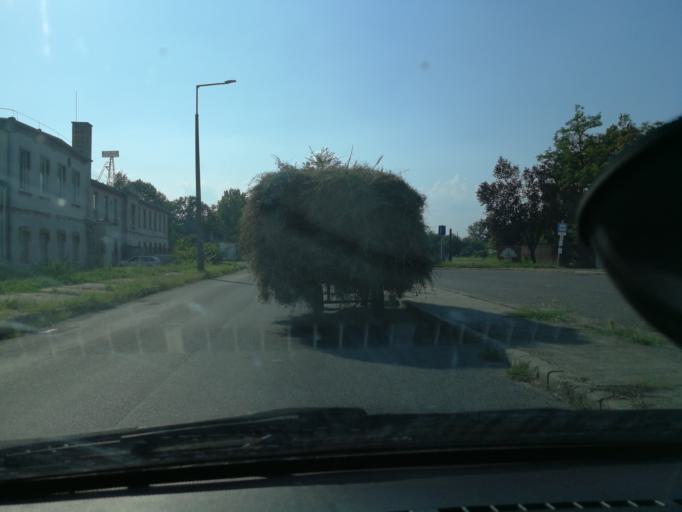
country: HU
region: Bacs-Kiskun
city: Kalocsa
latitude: 46.5345
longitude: 18.9949
